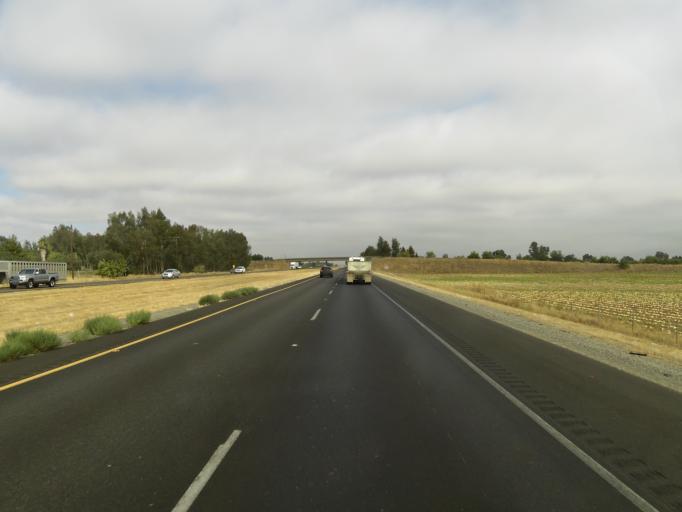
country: US
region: California
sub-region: Yolo County
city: Dunnigan
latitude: 38.9082
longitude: -121.9886
